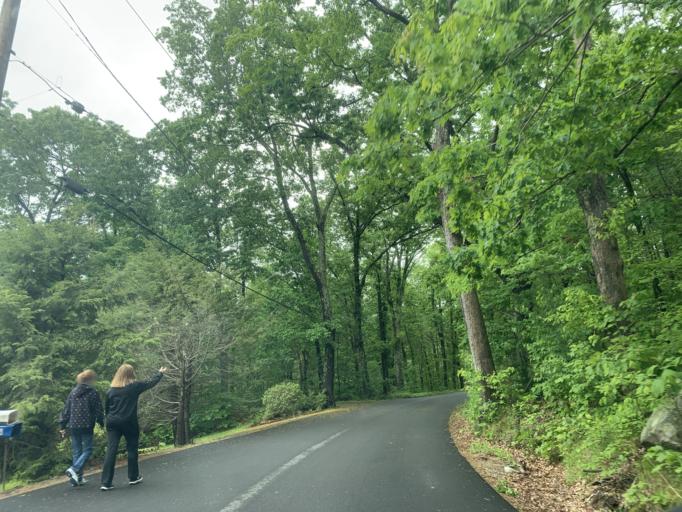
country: US
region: Massachusetts
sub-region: Worcester County
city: Upton
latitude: 42.1807
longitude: -71.6206
